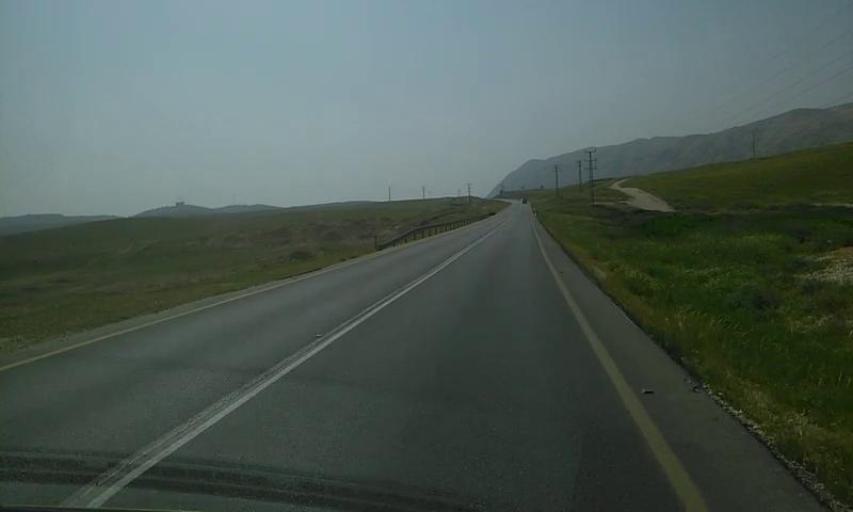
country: PS
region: West Bank
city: An Nuway`imah
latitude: 31.9116
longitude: 35.4218
